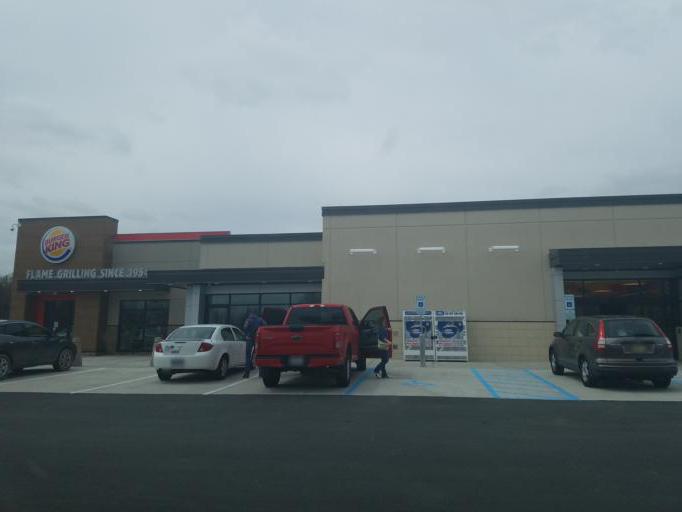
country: US
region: Ohio
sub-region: Trumbull County
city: Lordstown
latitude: 41.1045
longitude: -80.8880
